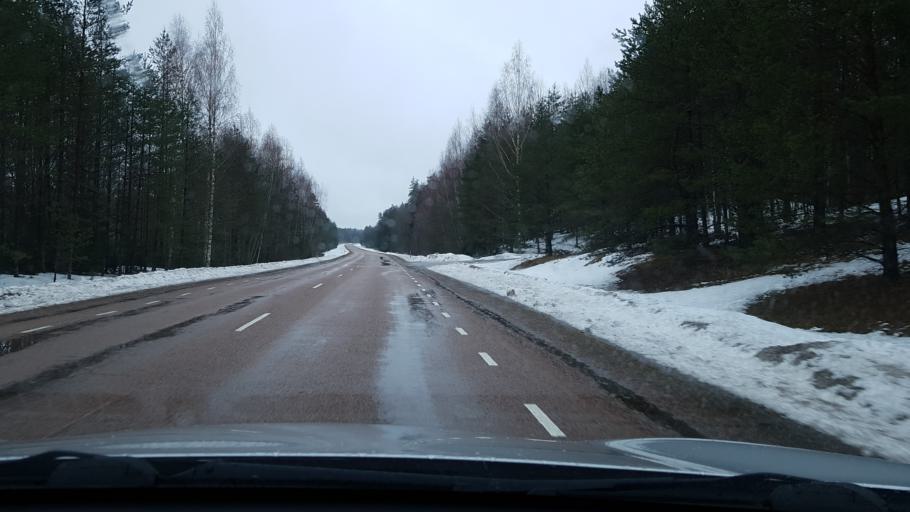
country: EE
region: Vorumaa
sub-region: Voru linn
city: Voru
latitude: 57.7702
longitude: 26.8589
